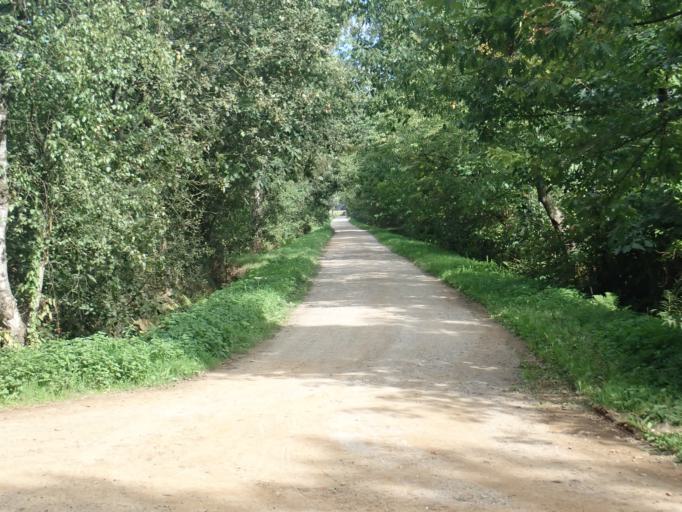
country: BE
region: Flanders
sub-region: Provincie Antwerpen
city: Beerse
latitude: 51.3081
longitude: 4.8017
